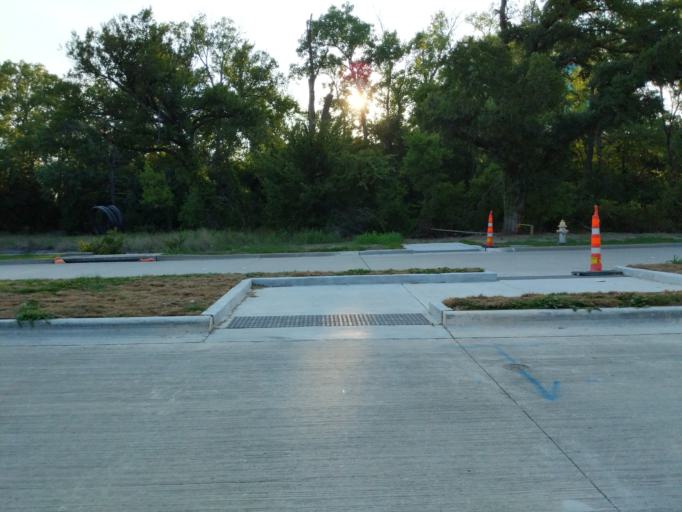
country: US
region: Texas
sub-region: Collin County
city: Plano
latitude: 32.9925
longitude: -96.7067
